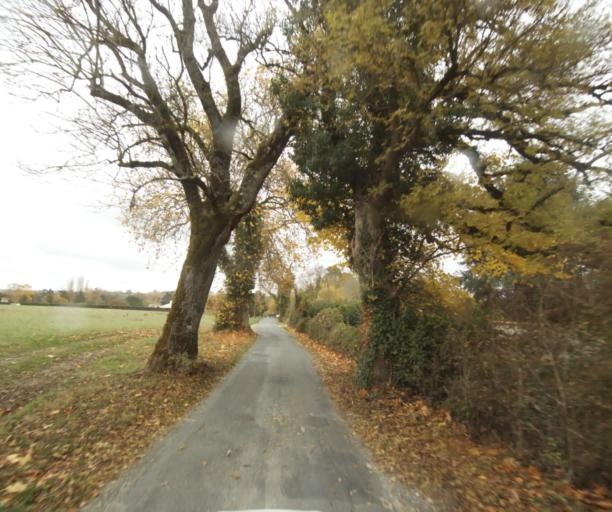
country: FR
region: Poitou-Charentes
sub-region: Departement de la Charente-Maritime
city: Saintes
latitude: 45.7610
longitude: -0.6321
